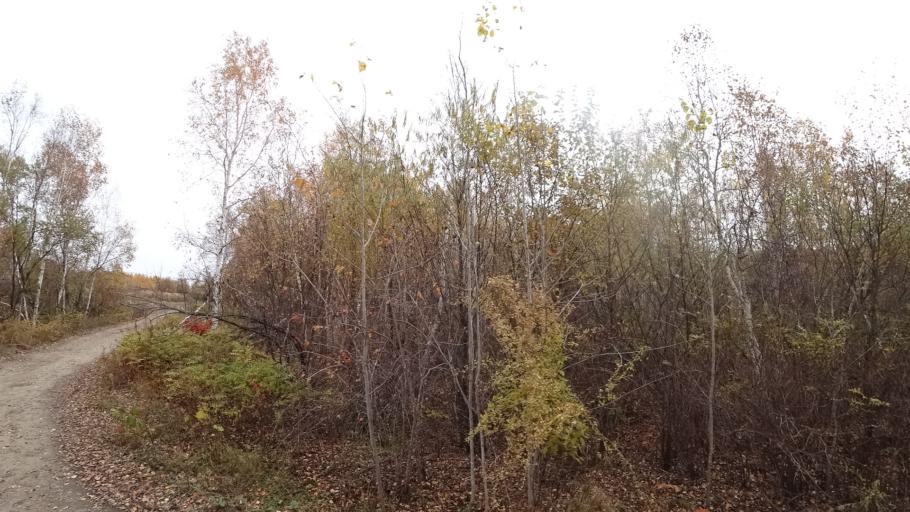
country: RU
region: Khabarovsk Krai
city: Amursk
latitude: 50.1518
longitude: 136.9915
